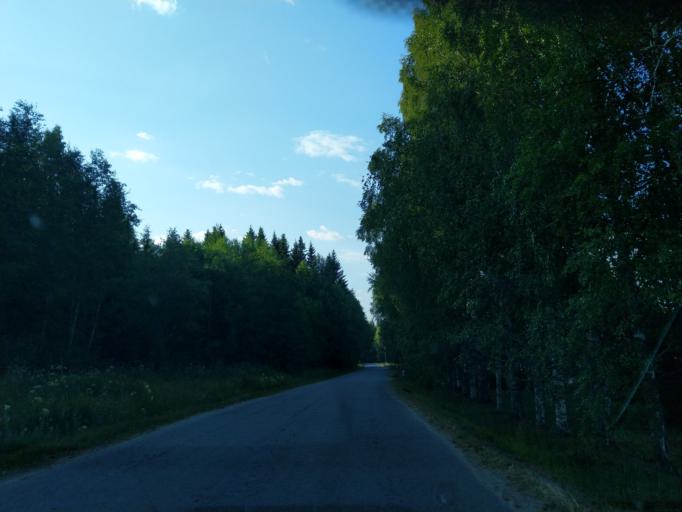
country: FI
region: Satakunta
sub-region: Pori
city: Laengelmaeki
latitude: 61.8054
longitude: 22.1907
